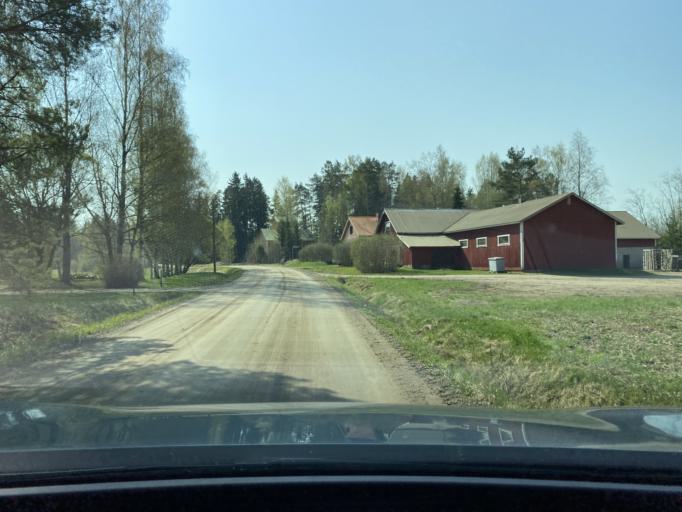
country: FI
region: Satakunta
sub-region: Pori
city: Huittinen
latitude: 61.1370
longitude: 22.8332
